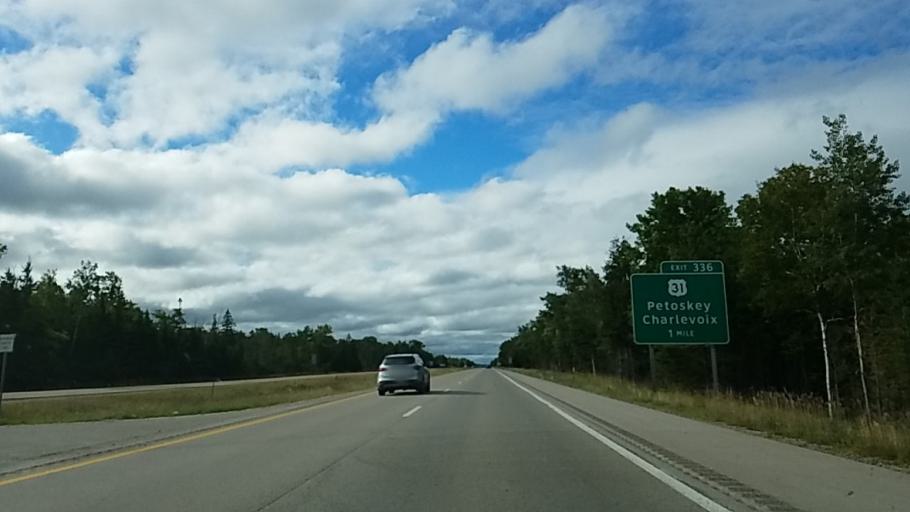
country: US
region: Michigan
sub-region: Mackinac County
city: Saint Ignace
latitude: 45.7516
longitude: -84.7290
